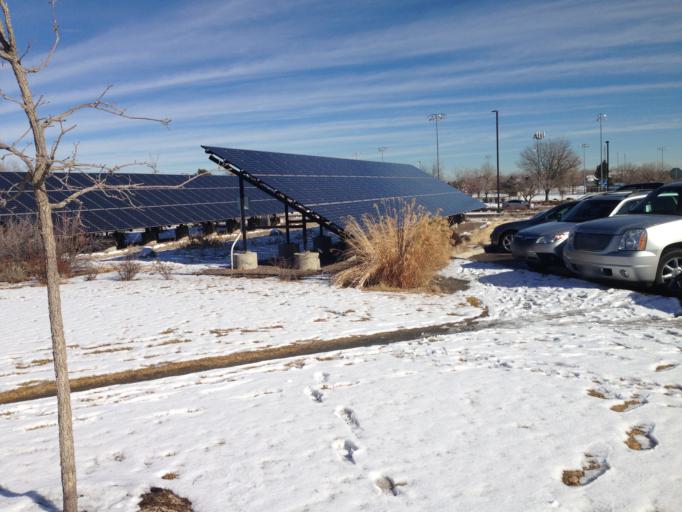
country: US
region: Colorado
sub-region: Broomfield County
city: Broomfield
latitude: 39.9174
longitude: -105.0683
